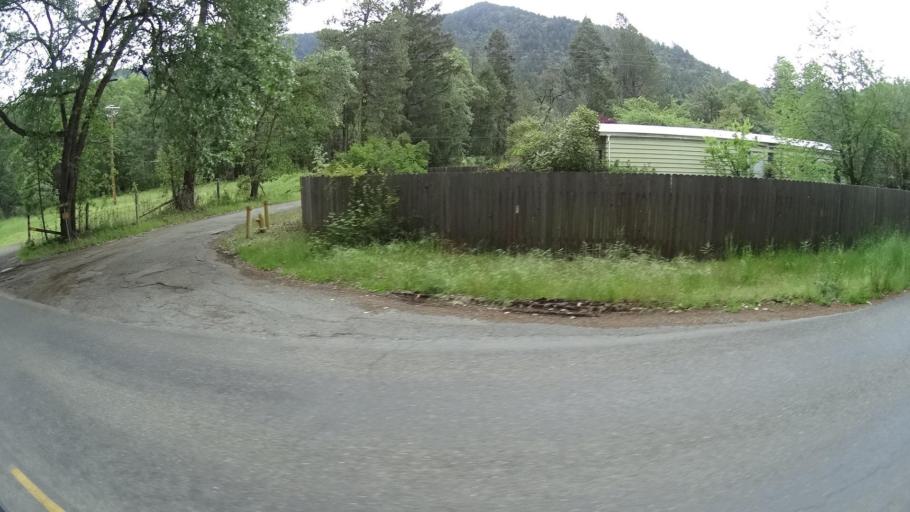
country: US
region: California
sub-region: Humboldt County
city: Willow Creek
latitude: 40.9577
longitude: -123.6297
